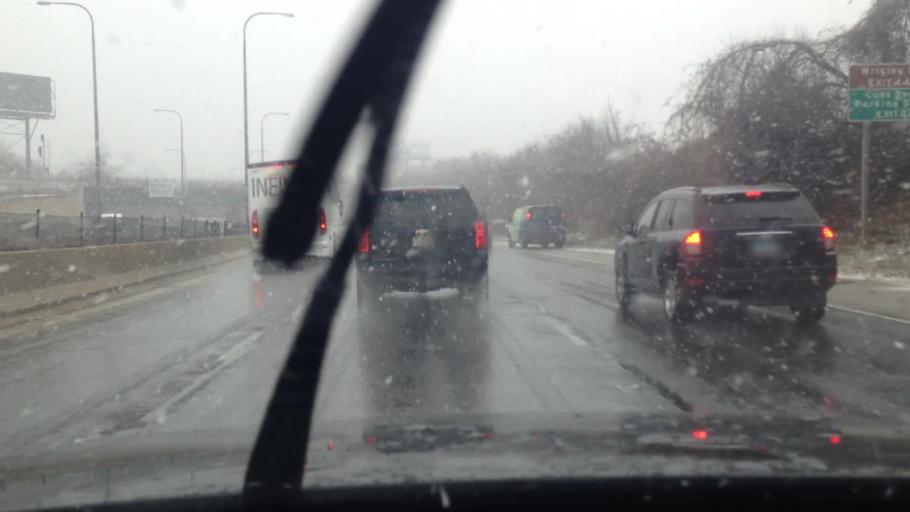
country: US
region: Illinois
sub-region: Cook County
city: Lincolnwood
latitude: 41.9643
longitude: -87.7502
